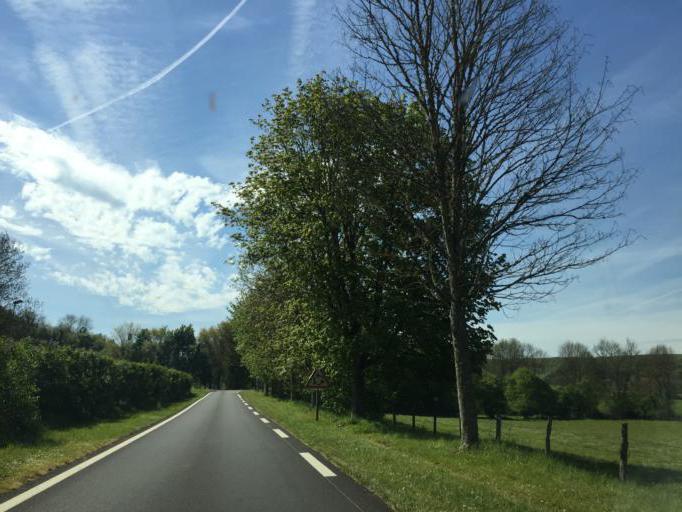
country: FR
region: Bourgogne
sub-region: Departement de la Nievre
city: Clamecy
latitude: 47.4540
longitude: 3.5506
